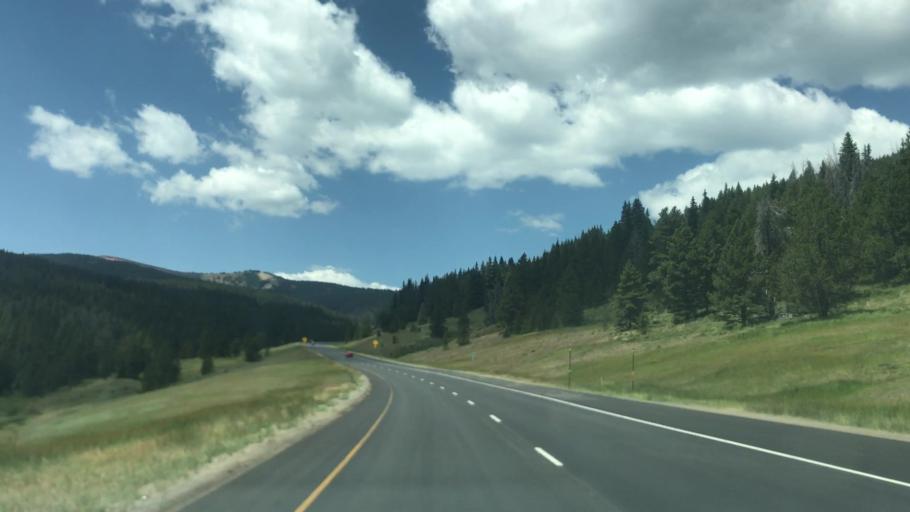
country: US
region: Colorado
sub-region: Summit County
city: Frisco
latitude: 39.5070
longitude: -106.1901
